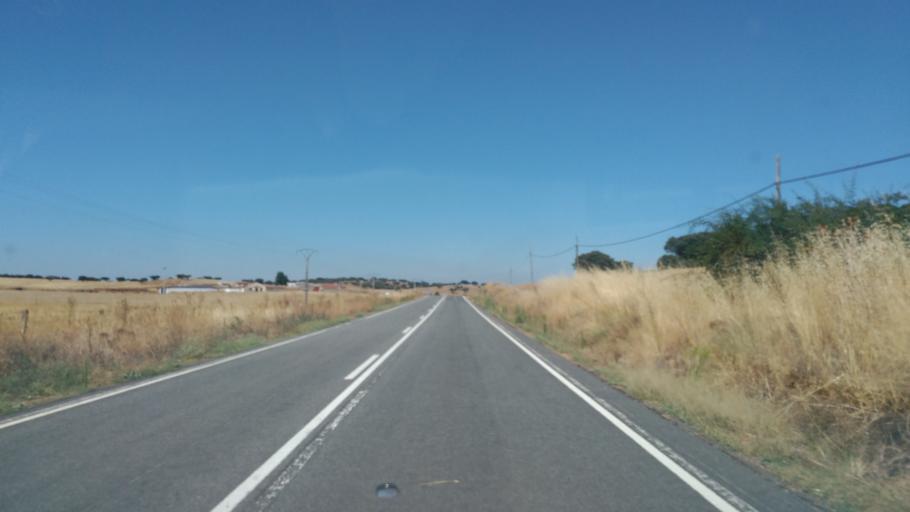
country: ES
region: Castille and Leon
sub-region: Provincia de Salamanca
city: Vecinos
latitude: 40.7936
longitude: -5.9130
